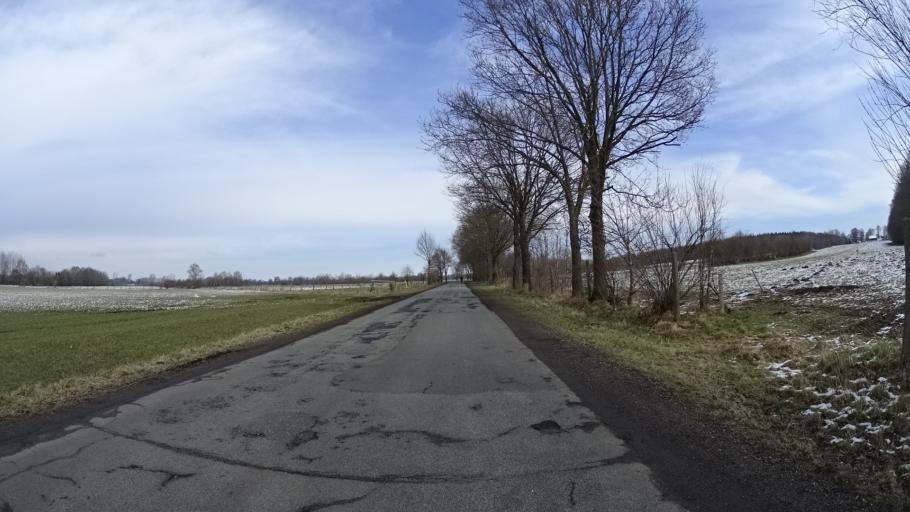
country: DE
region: Schleswig-Holstein
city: Gonnebek
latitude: 54.0482
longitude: 10.1305
